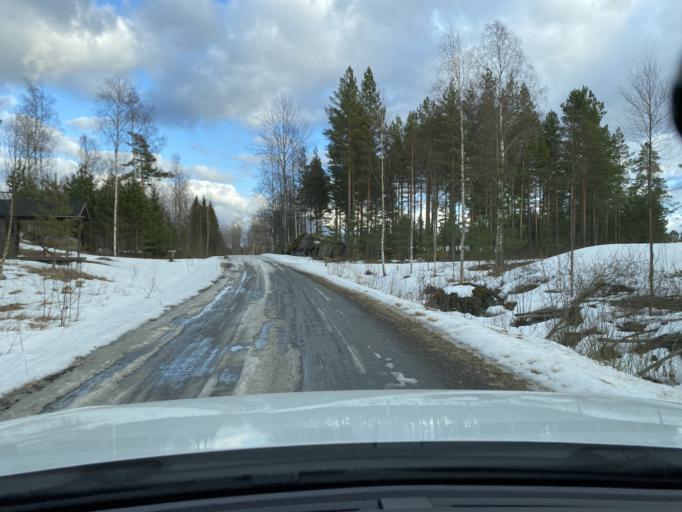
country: FI
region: Pirkanmaa
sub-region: Lounais-Pirkanmaa
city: Mouhijaervi
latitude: 61.4304
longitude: 22.9922
